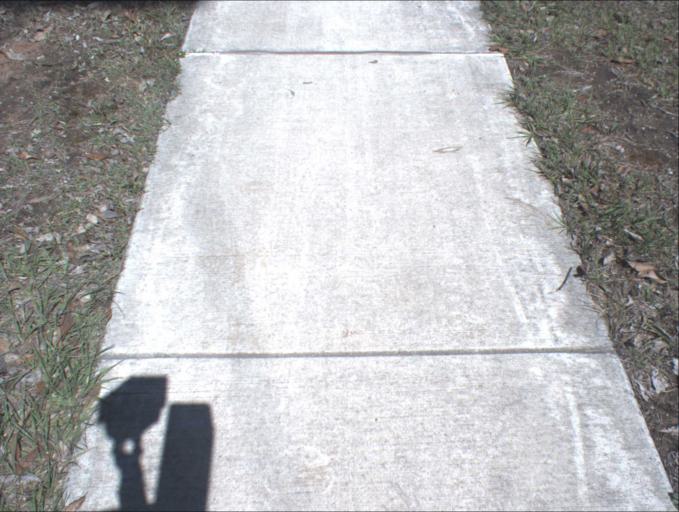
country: AU
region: Queensland
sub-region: Logan
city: Chambers Flat
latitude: -27.7446
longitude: 153.0536
